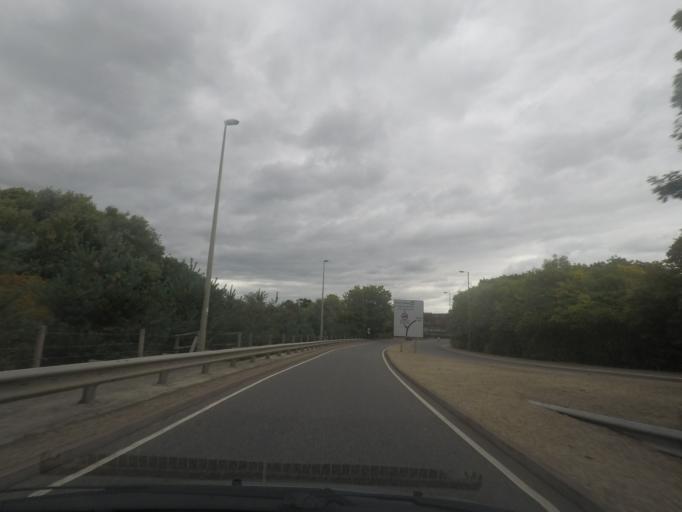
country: GB
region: England
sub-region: Oxfordshire
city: Harwell
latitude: 51.6215
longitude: -1.3039
